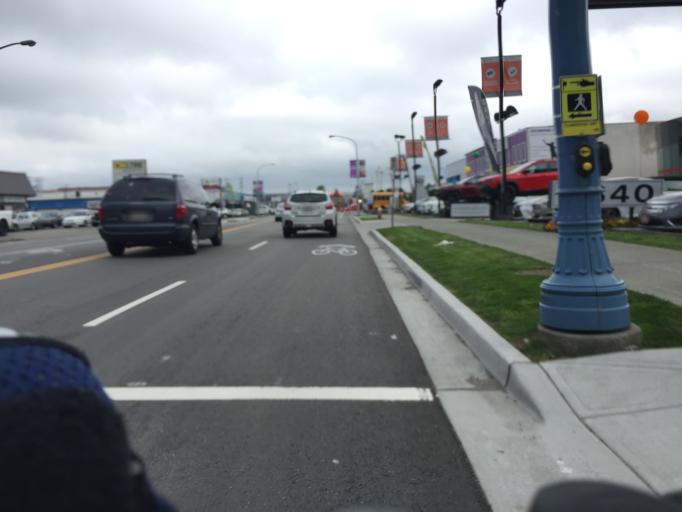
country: CA
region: British Columbia
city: Richmond
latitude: 49.1720
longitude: -123.1401
